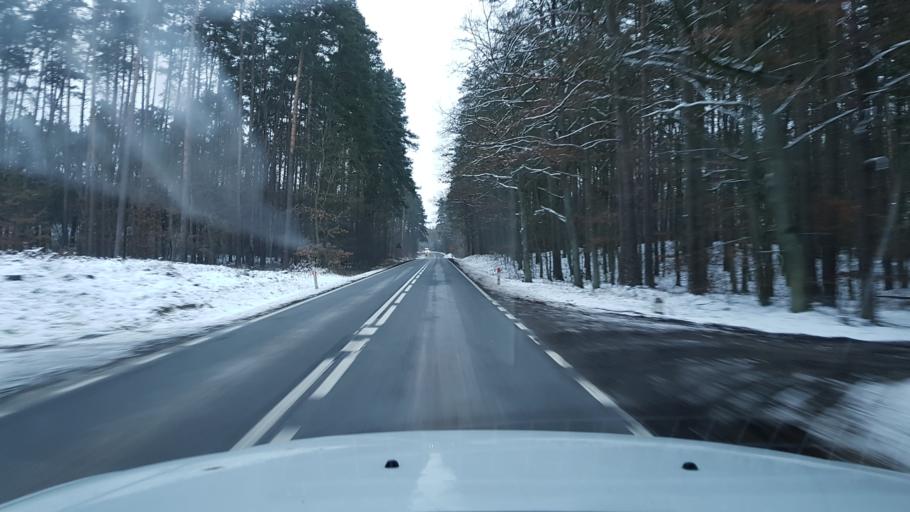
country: PL
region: West Pomeranian Voivodeship
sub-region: Powiat gryfinski
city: Chojna
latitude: 53.0468
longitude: 14.4537
